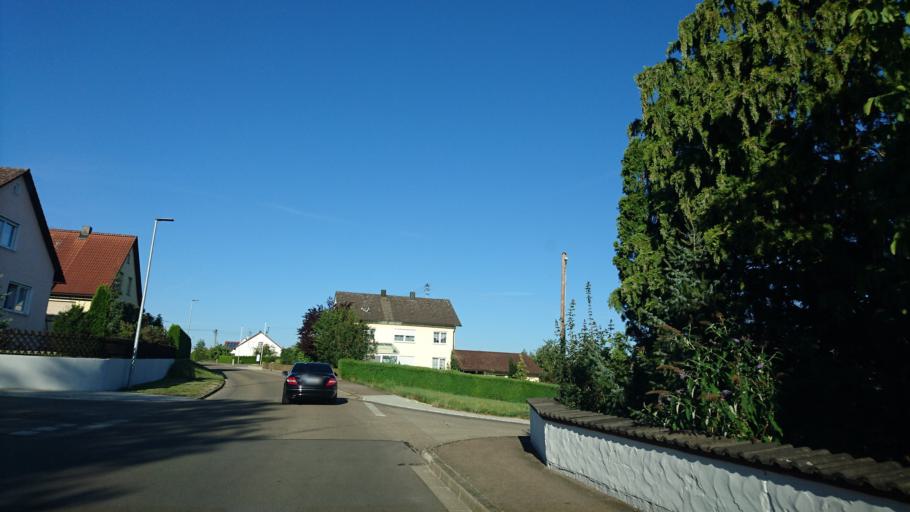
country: DE
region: Bavaria
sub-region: Swabia
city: Funfstetten
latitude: 48.8322
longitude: 10.7723
